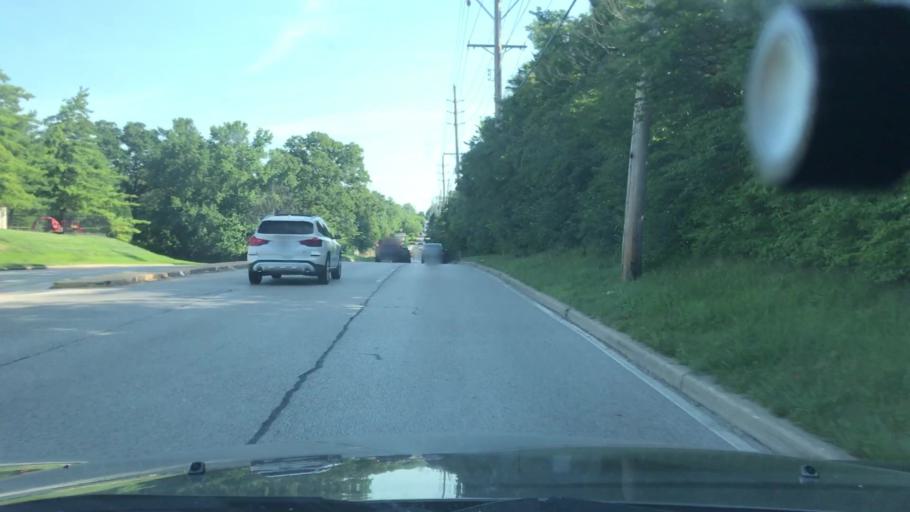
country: US
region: Missouri
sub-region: Saint Louis County
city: Creve Coeur
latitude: 38.6469
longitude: -90.4433
